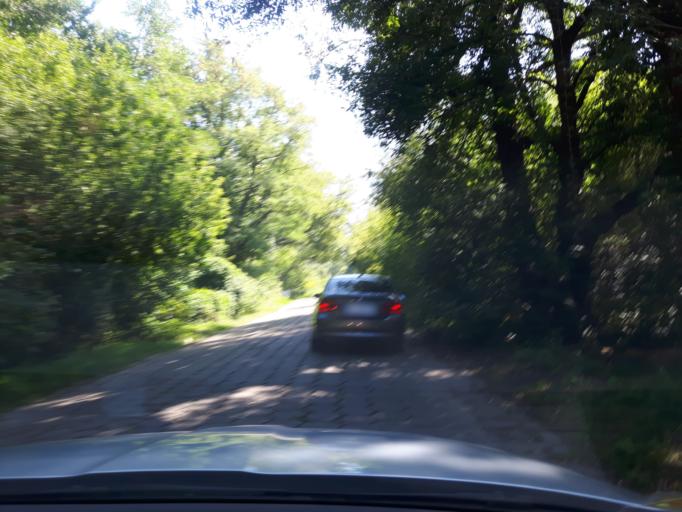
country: PL
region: Masovian Voivodeship
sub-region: Powiat wolominski
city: Zabki
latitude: 52.2727
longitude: 21.0921
